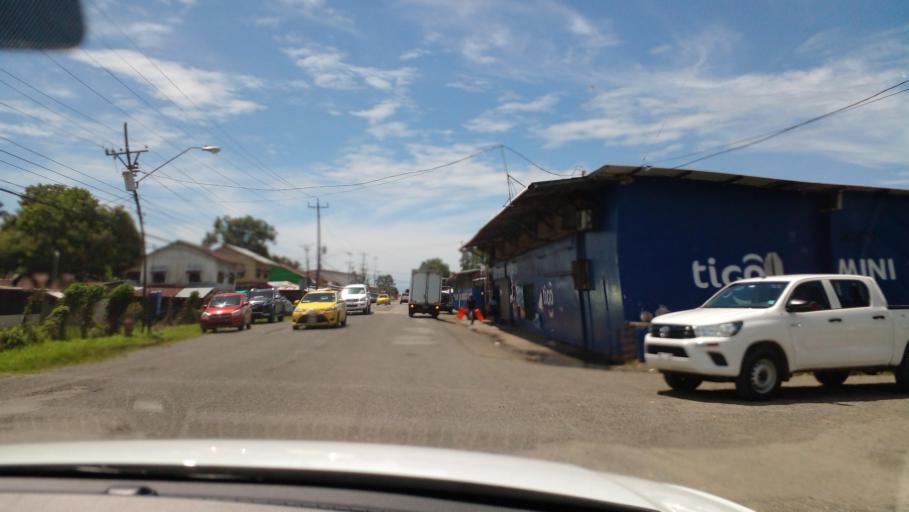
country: PA
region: Bocas del Toro
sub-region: Distrito de Changuinola
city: Changuinola
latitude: 9.4205
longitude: -82.5202
